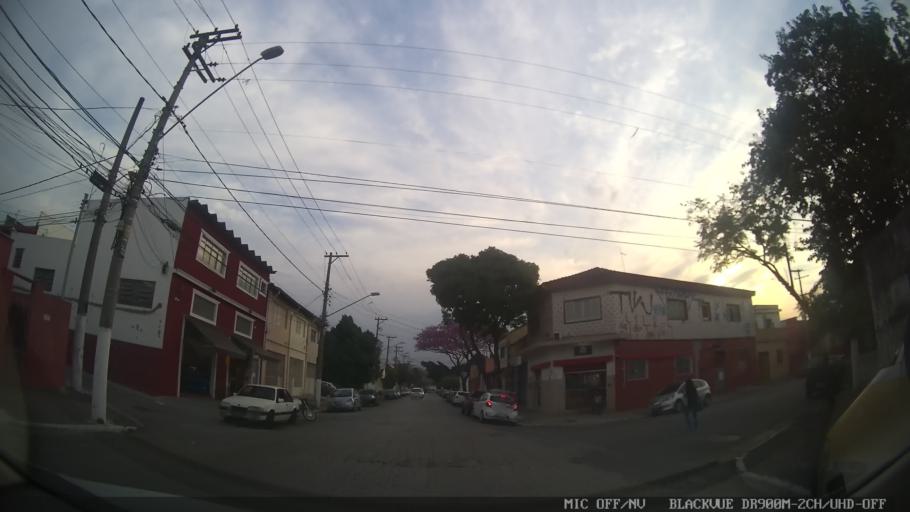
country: BR
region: Sao Paulo
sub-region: Sao Caetano Do Sul
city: Sao Caetano do Sul
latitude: -23.6007
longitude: -46.5888
